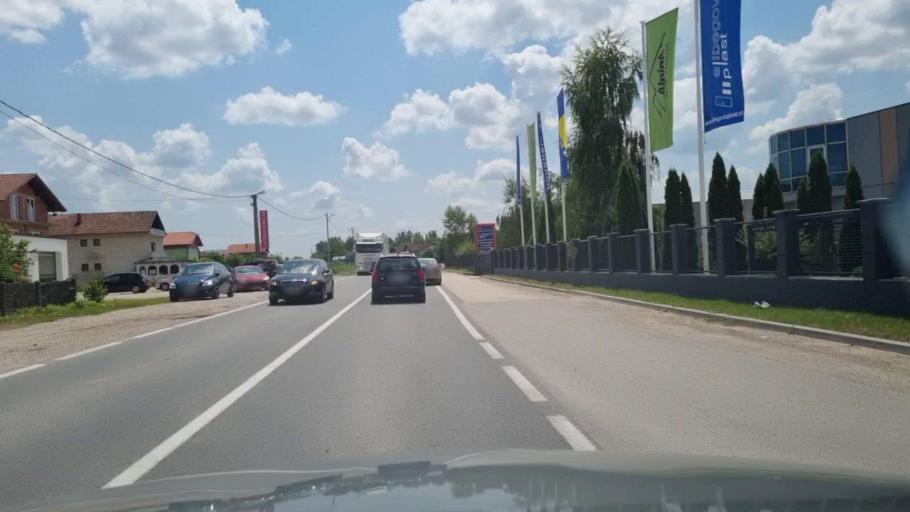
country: BA
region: Federation of Bosnia and Herzegovina
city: Gracanica
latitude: 44.6710
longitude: 18.3329
